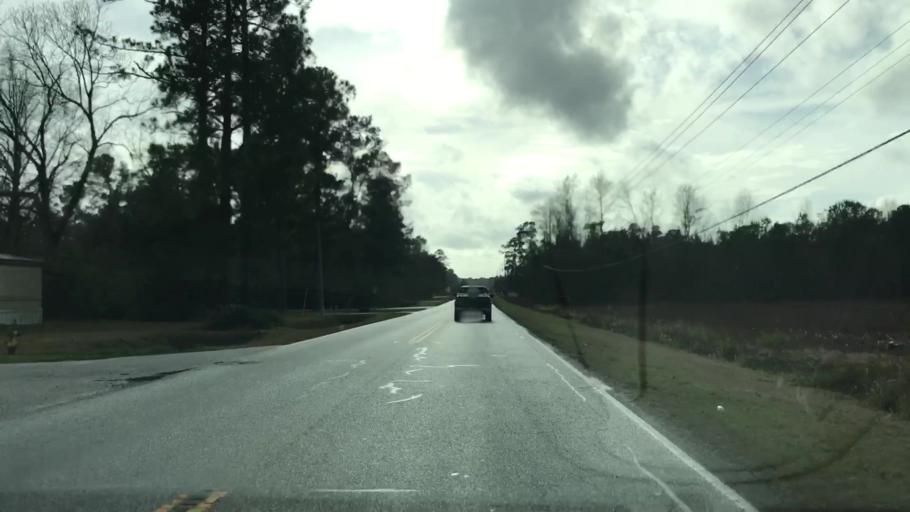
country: US
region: South Carolina
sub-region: Williamsburg County
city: Andrews
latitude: 33.4520
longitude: -79.5816
